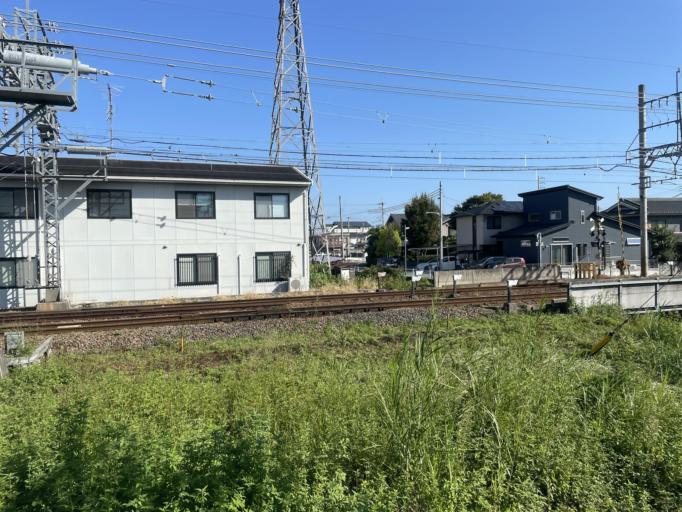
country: JP
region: Nara
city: Gose
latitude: 34.5086
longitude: 135.7239
